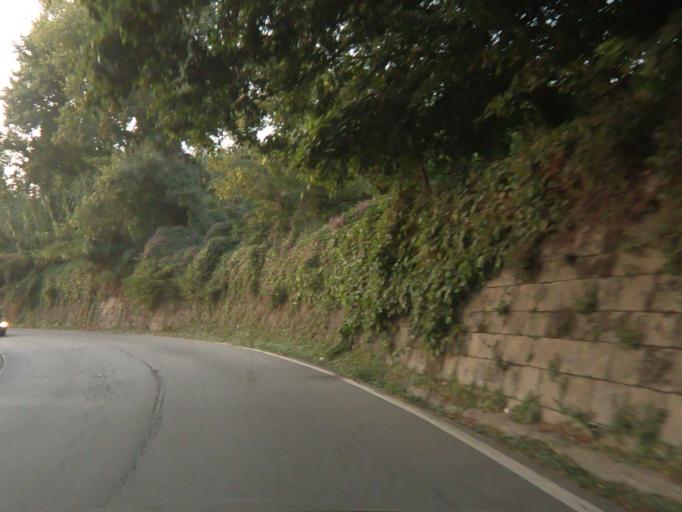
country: PT
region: Porto
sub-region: Gondomar
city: Valbom
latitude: 41.1408
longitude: -8.5718
